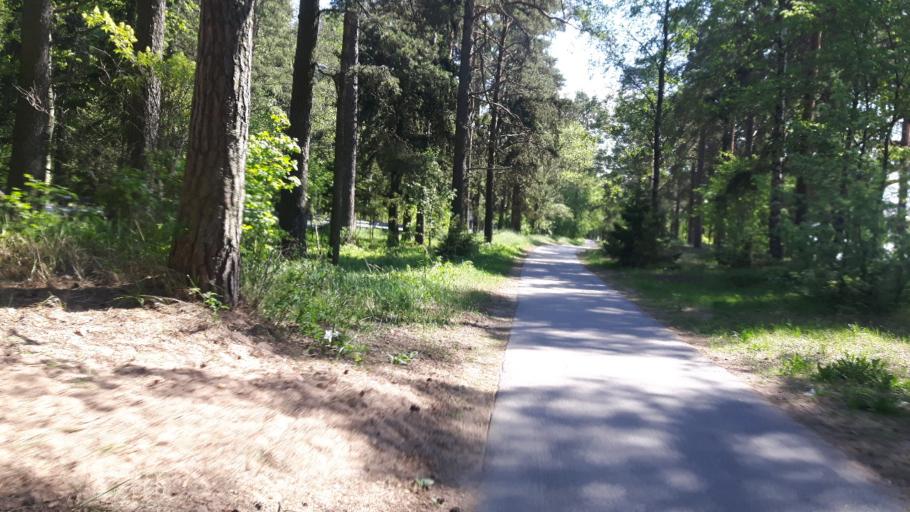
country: RU
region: St.-Petersburg
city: Komarovo
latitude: 60.1747
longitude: 29.8009
